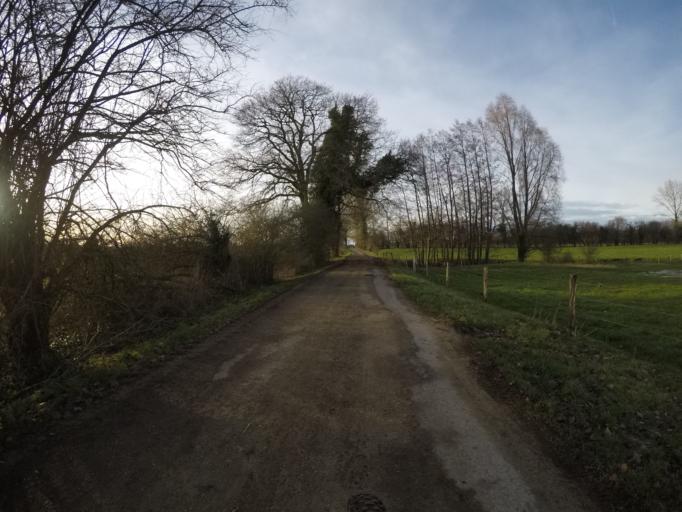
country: BE
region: Wallonia
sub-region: Province du Luxembourg
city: Tintigny
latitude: 49.6675
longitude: 5.4575
